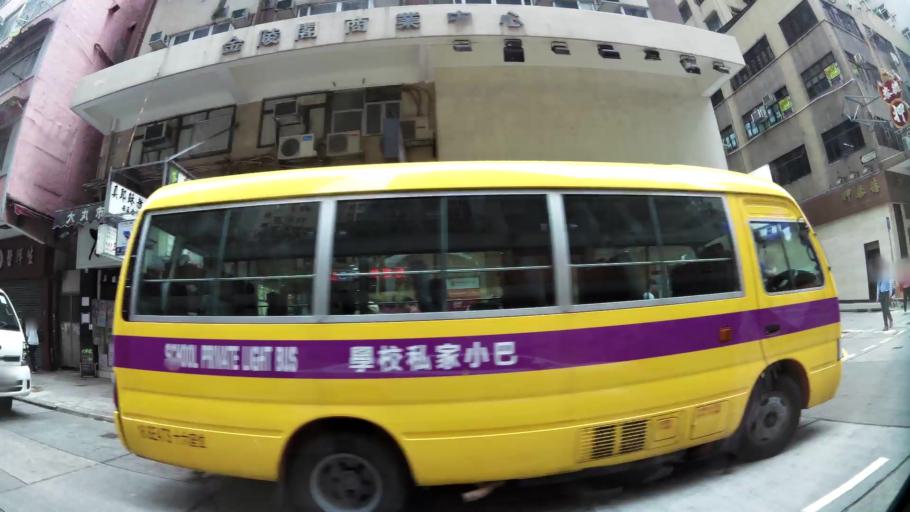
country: HK
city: Hong Kong
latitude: 22.2862
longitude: 114.1343
